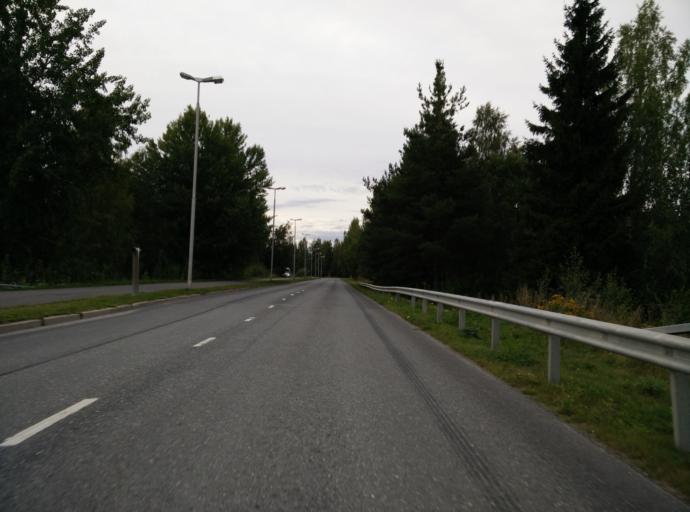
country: FI
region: Haeme
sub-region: Haemeenlinna
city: Haemeenlinna
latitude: 60.9924
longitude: 24.4852
